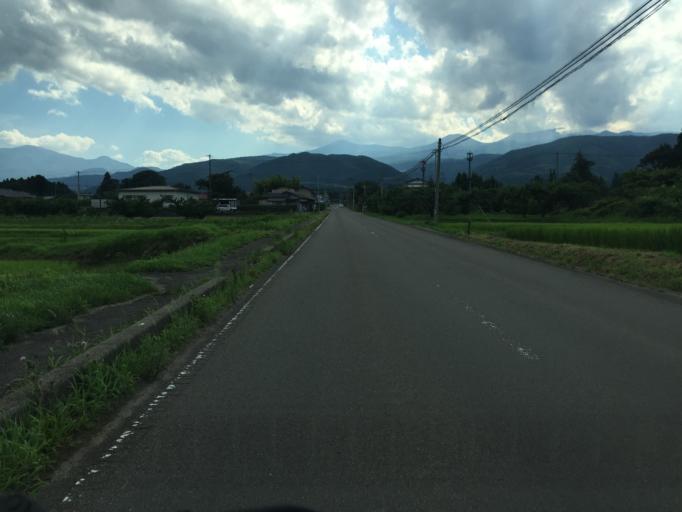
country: JP
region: Fukushima
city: Fukushima-shi
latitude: 37.7440
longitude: 140.3763
